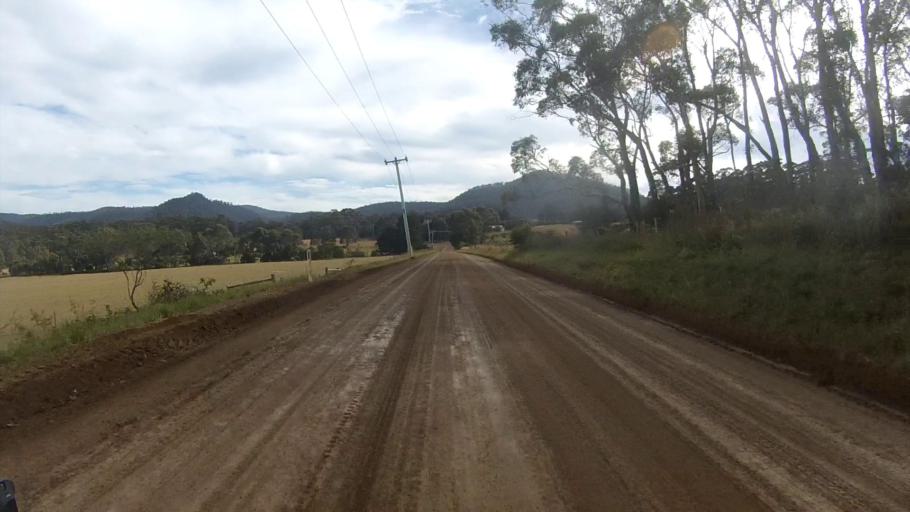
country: AU
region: Tasmania
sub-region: Sorell
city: Sorell
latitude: -42.7832
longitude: 147.8083
